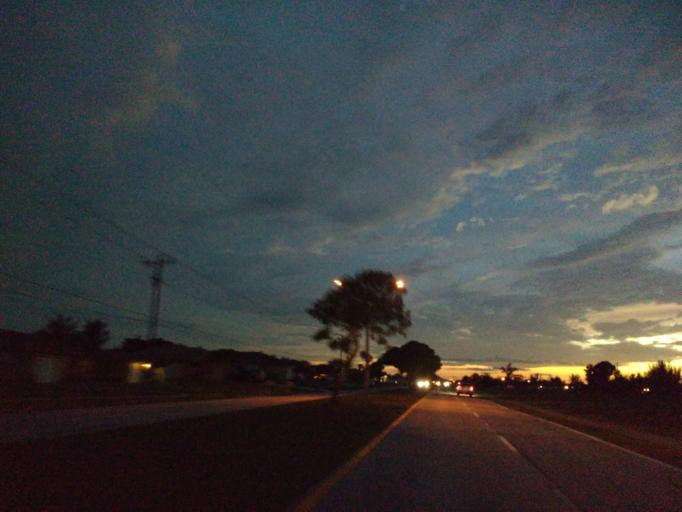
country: US
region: Florida
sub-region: Lee County
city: Cape Coral
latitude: 26.6230
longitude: -81.9931
